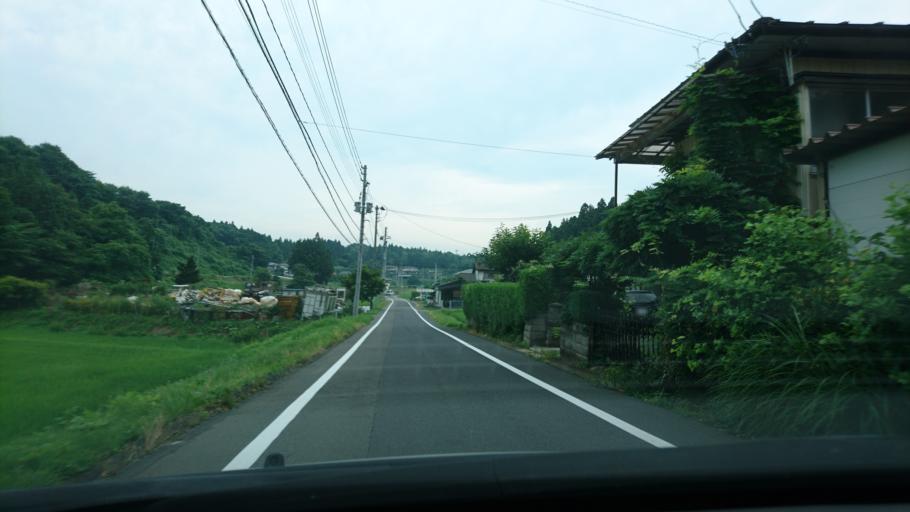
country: JP
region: Iwate
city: Ichinoseki
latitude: 38.9116
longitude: 141.1462
